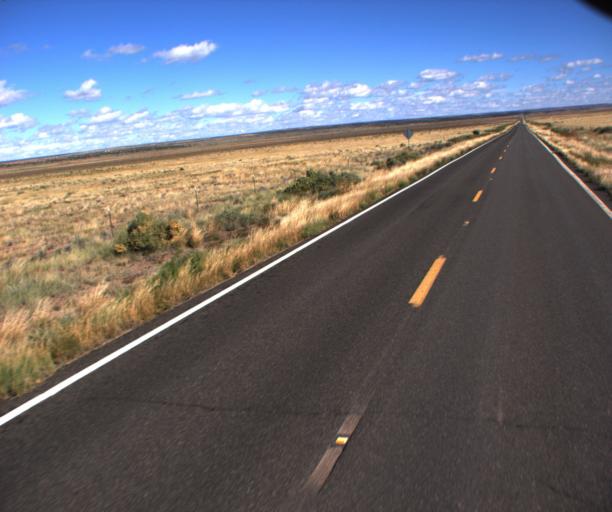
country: US
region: Arizona
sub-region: Apache County
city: Saint Johns
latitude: 34.6753
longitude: -109.2854
